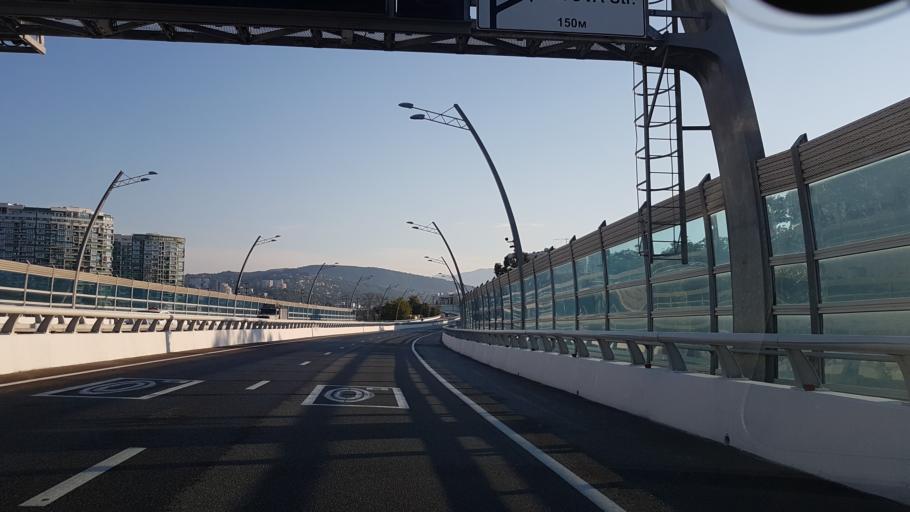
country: RU
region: Krasnodarskiy
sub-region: Sochi City
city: Sochi
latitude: 43.5914
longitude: 39.7304
